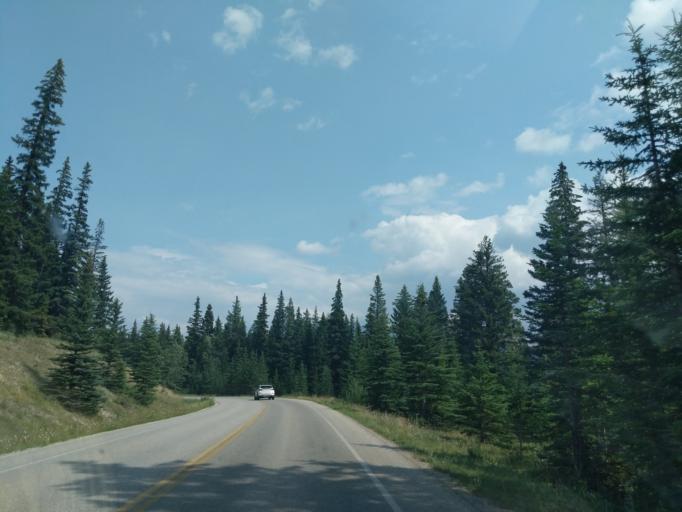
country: CA
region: Alberta
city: Banff
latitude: 51.1685
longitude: -115.6854
